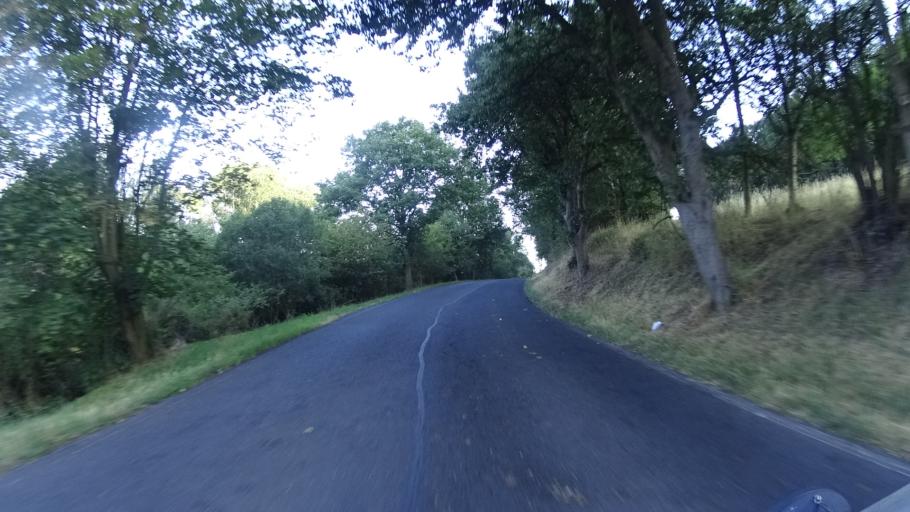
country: CZ
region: Ustecky
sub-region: Okres Litomerice
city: Litomerice
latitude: 50.5761
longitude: 14.0920
